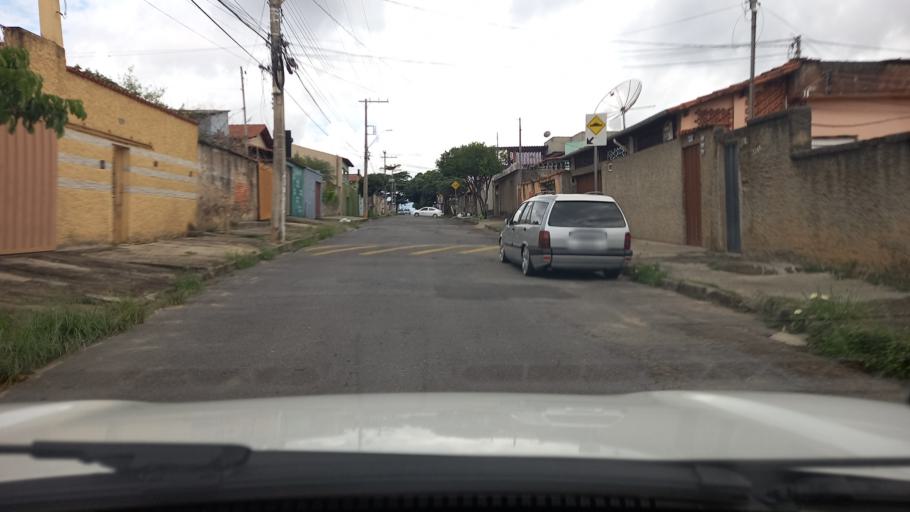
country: BR
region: Minas Gerais
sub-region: Contagem
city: Contagem
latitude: -19.9061
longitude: -44.0074
